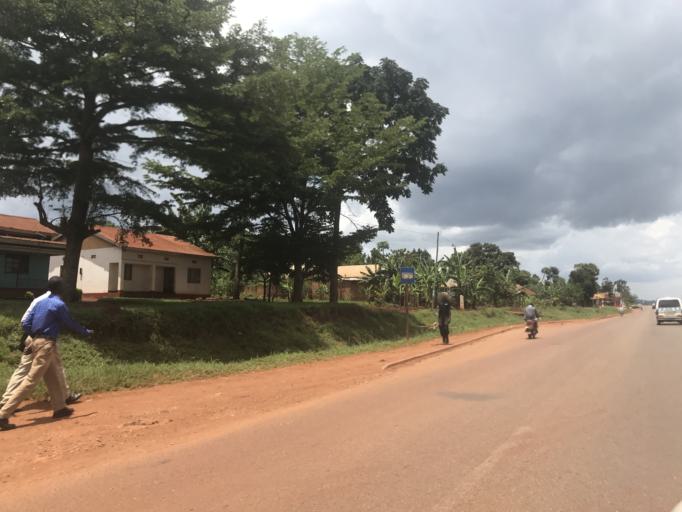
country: UG
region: Eastern Region
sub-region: Jinja District
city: Bugembe
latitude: 0.4717
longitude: 33.2528
